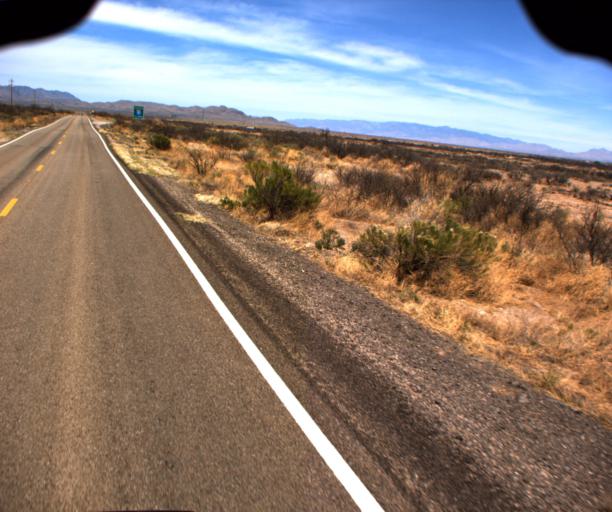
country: US
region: Arizona
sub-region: Cochise County
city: Willcox
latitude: 32.1661
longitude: -109.9442
